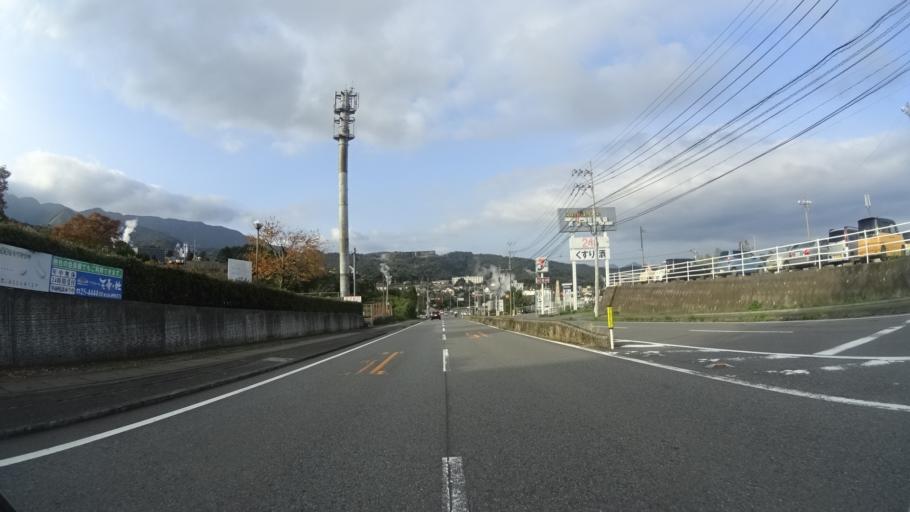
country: JP
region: Oita
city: Beppu
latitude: 33.3038
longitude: 131.4614
